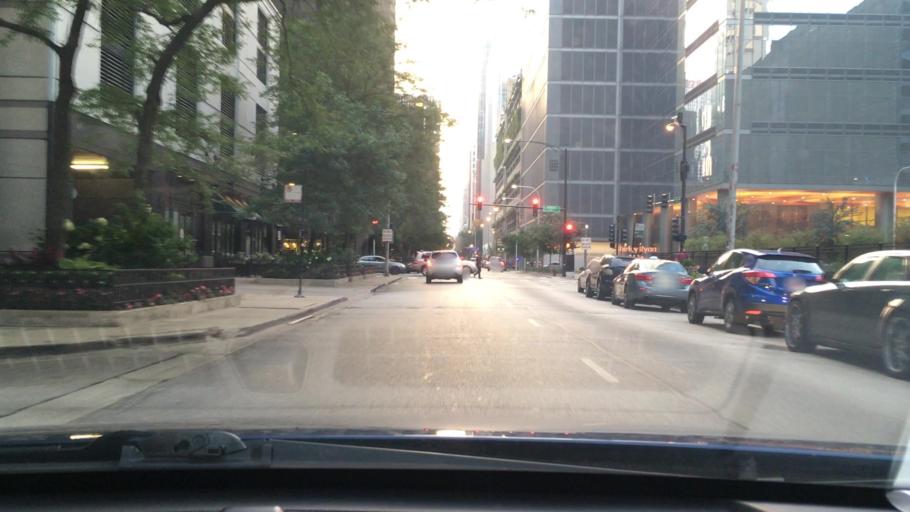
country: US
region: Illinois
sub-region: Cook County
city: Chicago
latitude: 41.8934
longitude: -87.6169
